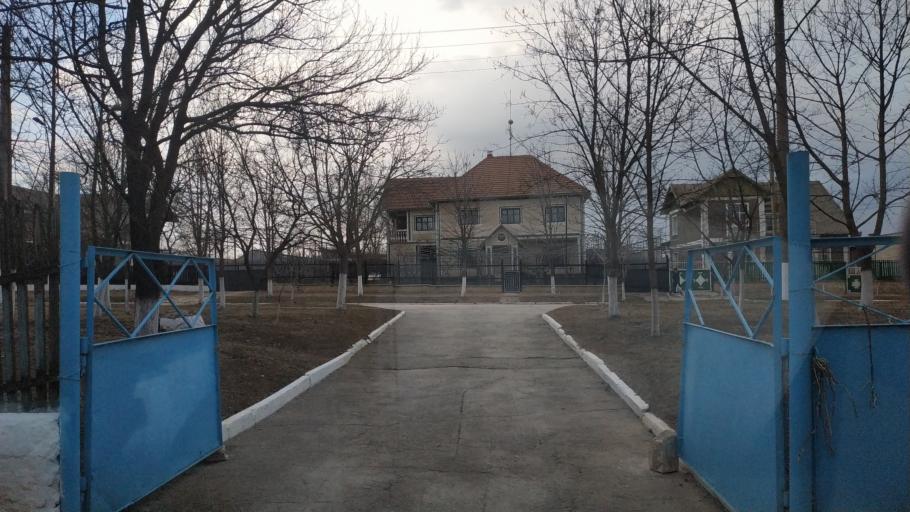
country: MD
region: Telenesti
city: Grigoriopol
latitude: 47.0122
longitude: 29.2908
